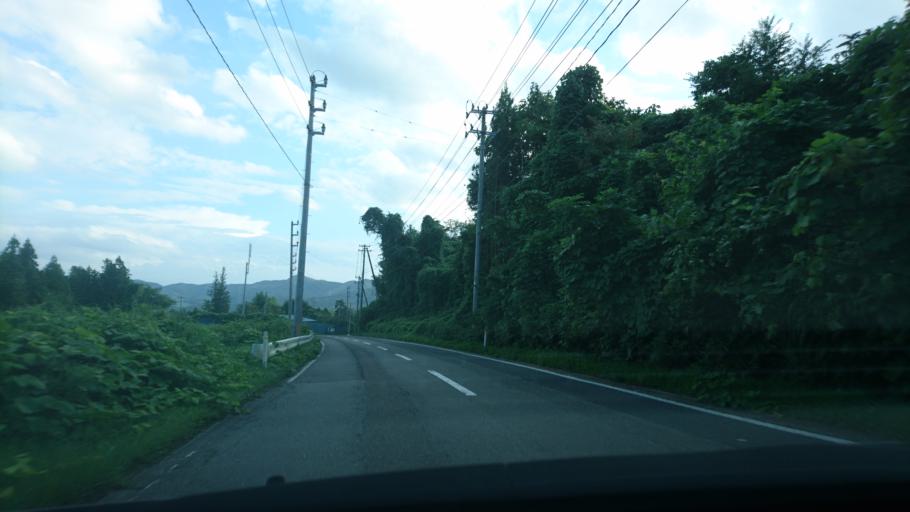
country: JP
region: Iwate
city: Ichinoseki
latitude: 39.0063
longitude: 141.2845
